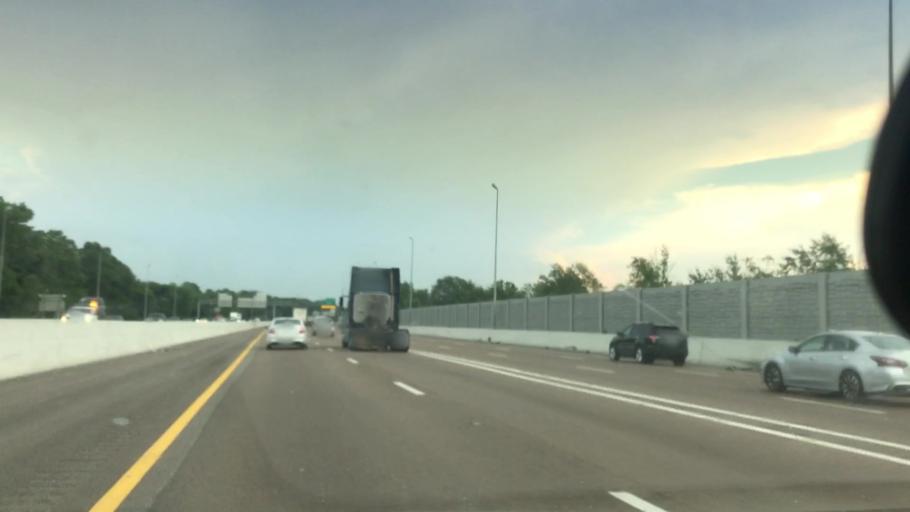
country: US
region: Tennessee
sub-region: Shelby County
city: Bartlett
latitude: 35.1468
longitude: -89.8780
